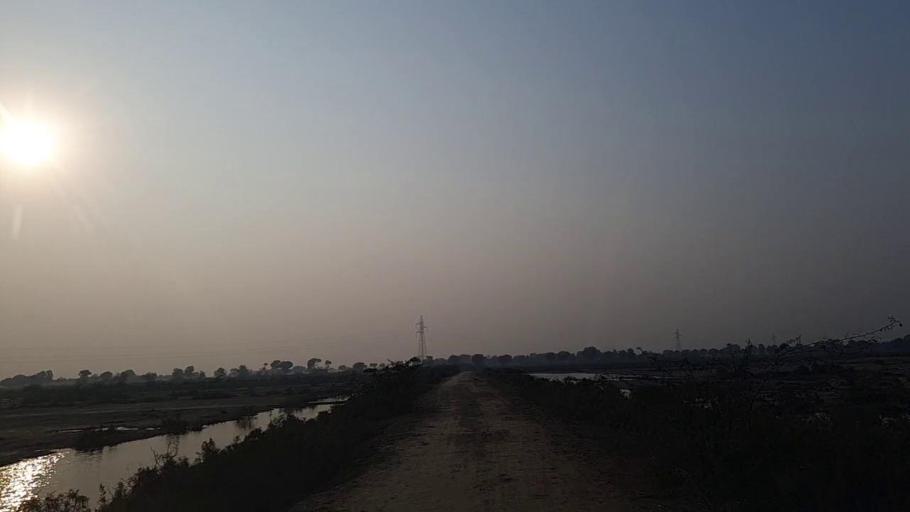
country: PK
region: Sindh
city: Nawabshah
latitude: 26.2358
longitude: 68.4697
